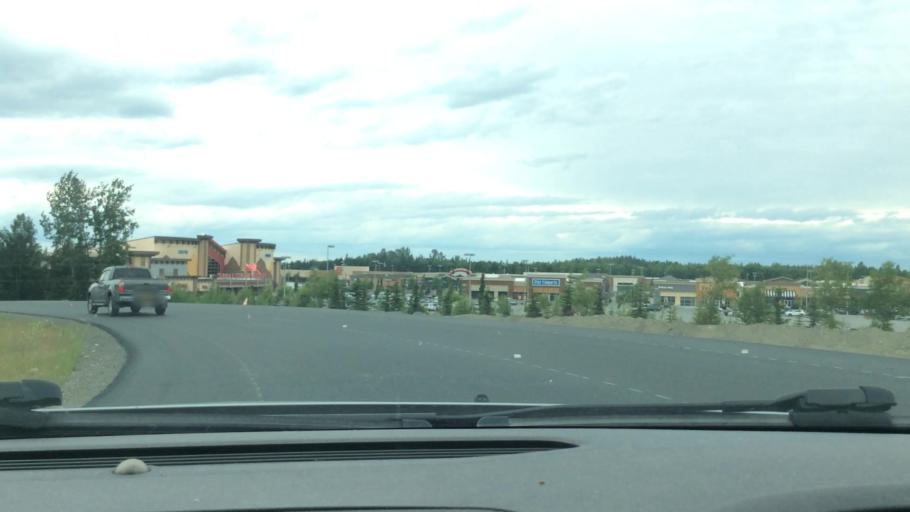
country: US
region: Alaska
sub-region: Anchorage Municipality
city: Elmendorf Air Force Base
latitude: 61.2280
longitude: -149.7359
